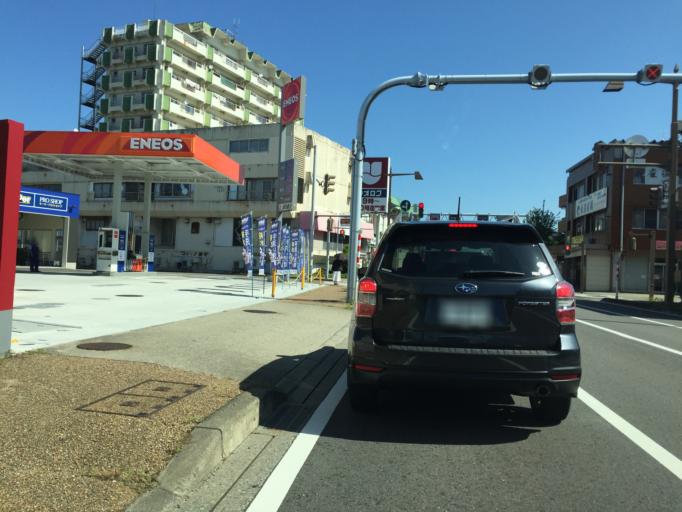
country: JP
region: Niigata
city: Niigata-shi
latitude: 37.9055
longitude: 139.0123
